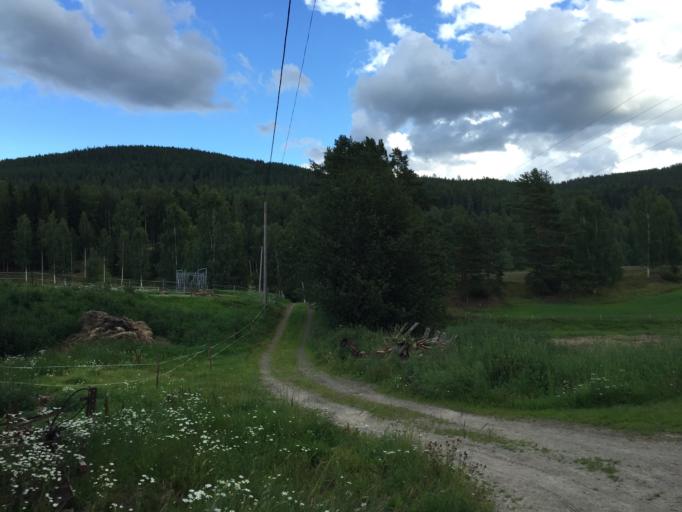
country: SE
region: Gaevleborg
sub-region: Ljusdals Kommun
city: Jaervsoe
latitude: 61.7456
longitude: 16.2722
